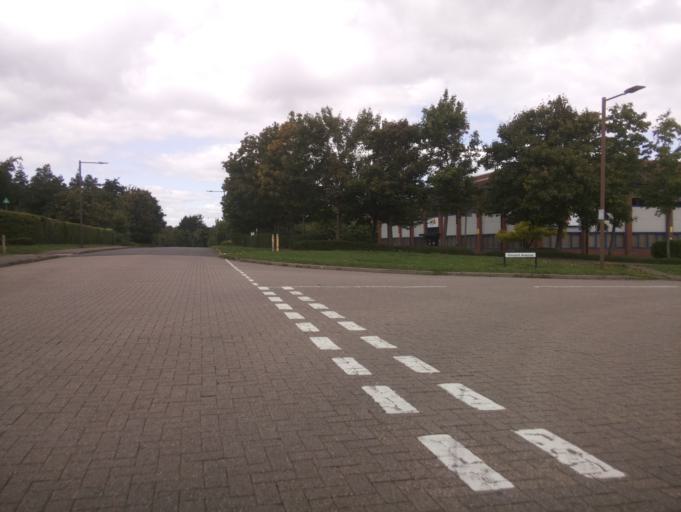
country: GB
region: England
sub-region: Milton Keynes
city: Shenley Church End
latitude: 52.0284
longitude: -0.8004
